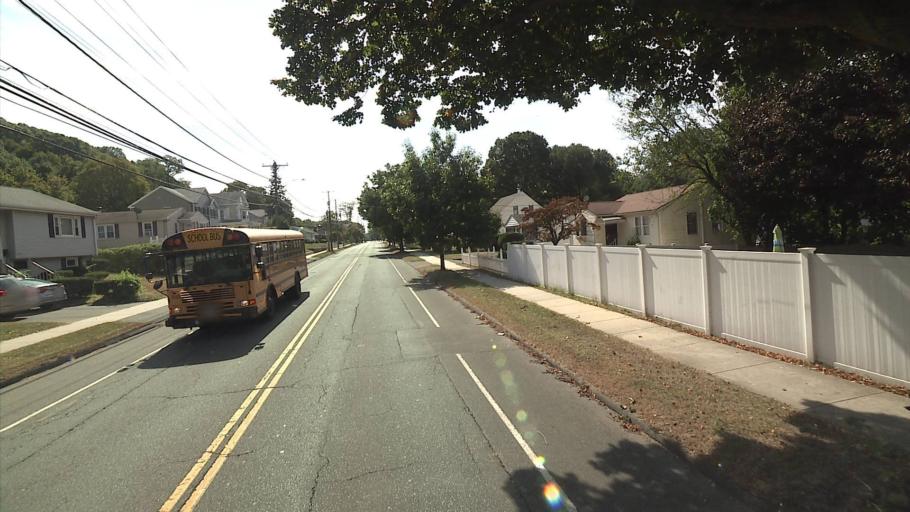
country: US
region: Connecticut
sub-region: New Haven County
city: East Haven
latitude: 41.3298
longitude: -72.8685
